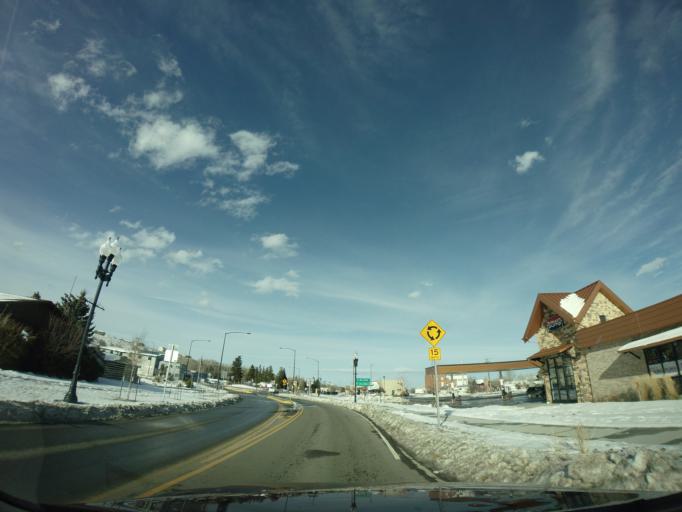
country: US
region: Montana
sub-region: Carbon County
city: Red Lodge
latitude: 45.1939
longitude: -109.2465
